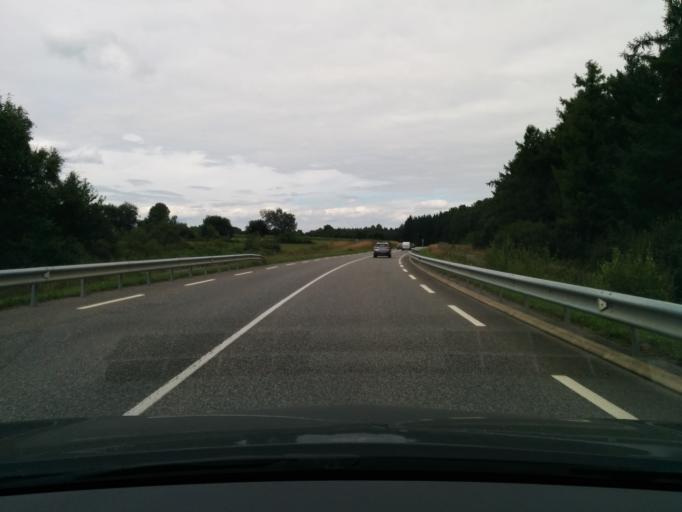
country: FR
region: Midi-Pyrenees
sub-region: Departement des Hautes-Pyrenees
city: La Barthe-de-Neste
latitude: 43.0670
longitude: 0.3591
